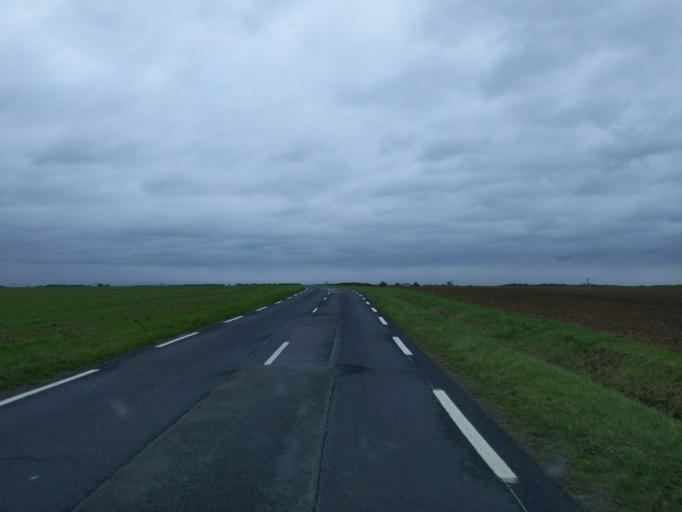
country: FR
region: Ile-de-France
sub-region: Departement des Yvelines
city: Cernay-la-Ville
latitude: 48.6651
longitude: 1.9878
